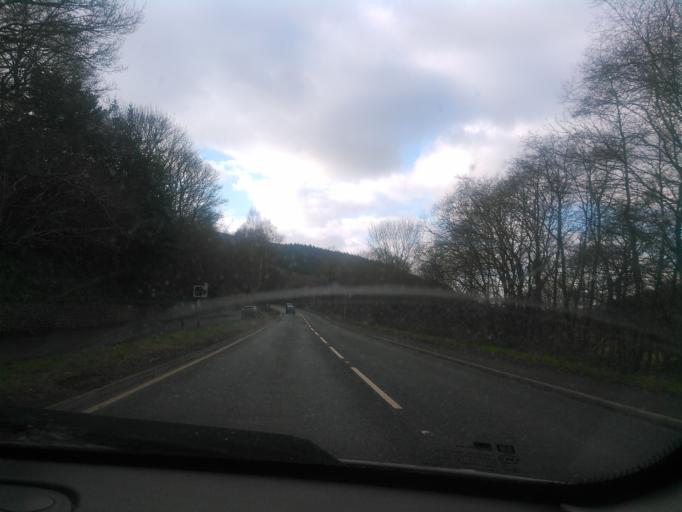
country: GB
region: Wales
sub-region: Denbighshire
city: Bryneglwys
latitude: 52.9786
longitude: -3.3223
